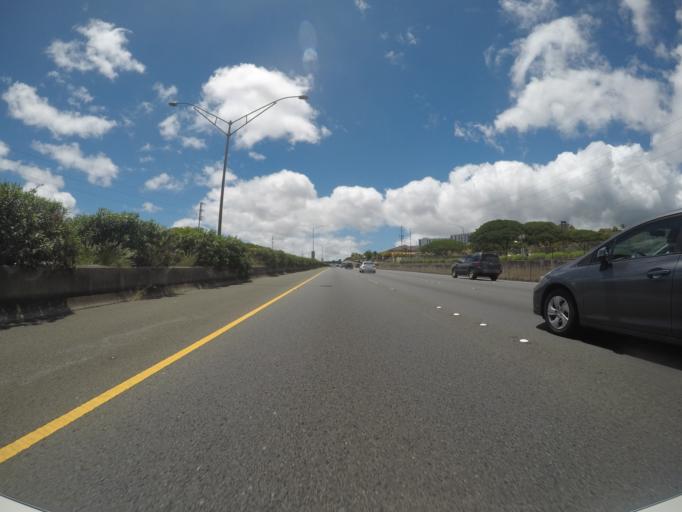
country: US
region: Hawaii
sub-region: Honolulu County
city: Halawa Heights
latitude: 21.3632
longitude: -157.9013
